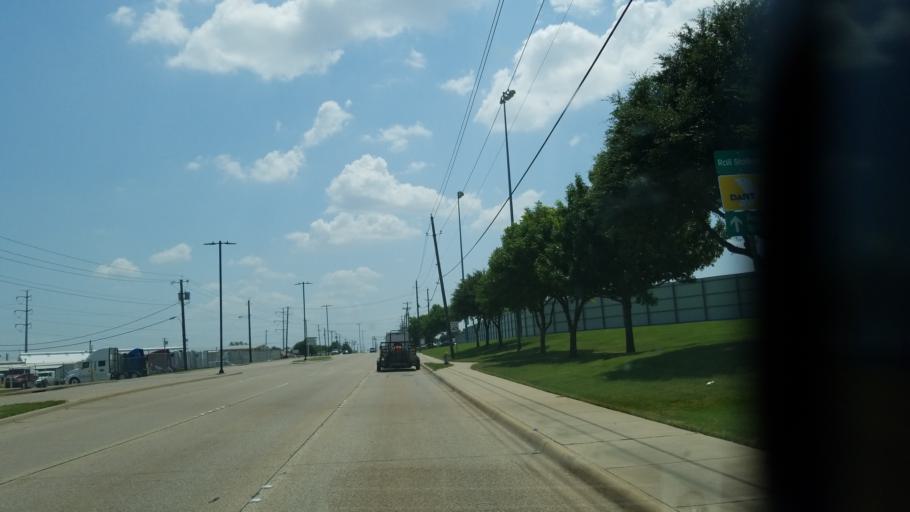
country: US
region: Texas
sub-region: Dallas County
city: Garland
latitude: 32.9253
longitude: -96.6308
